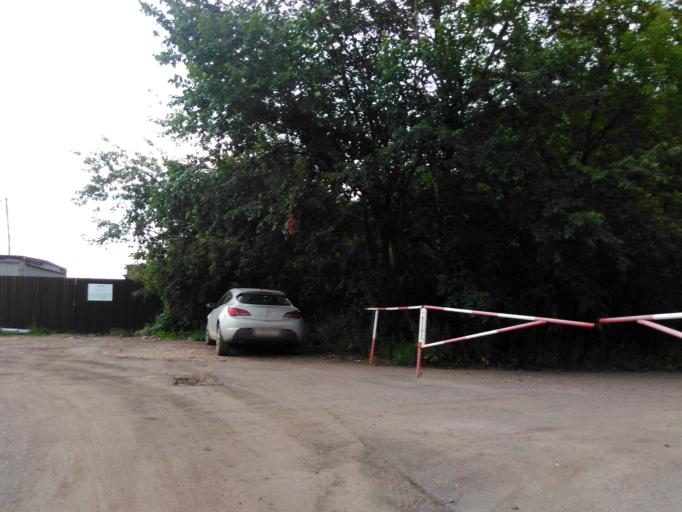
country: RU
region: Moskovskaya
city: Bogorodskoye
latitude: 55.8288
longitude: 37.7024
